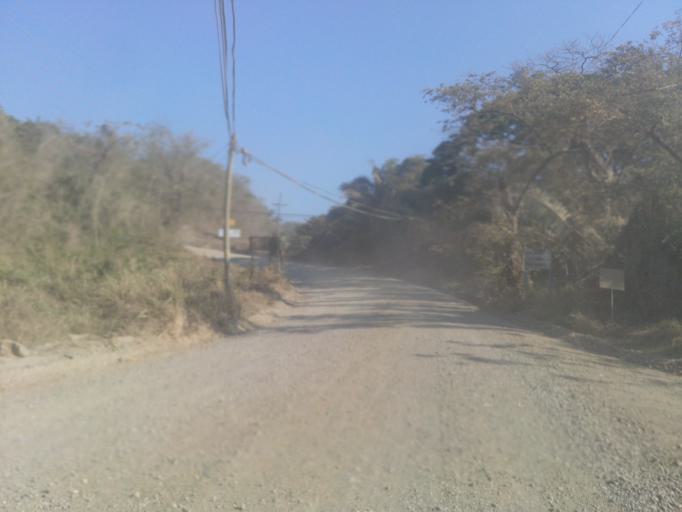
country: CR
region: Guanacaste
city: Samara
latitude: 9.9577
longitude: -85.6679
